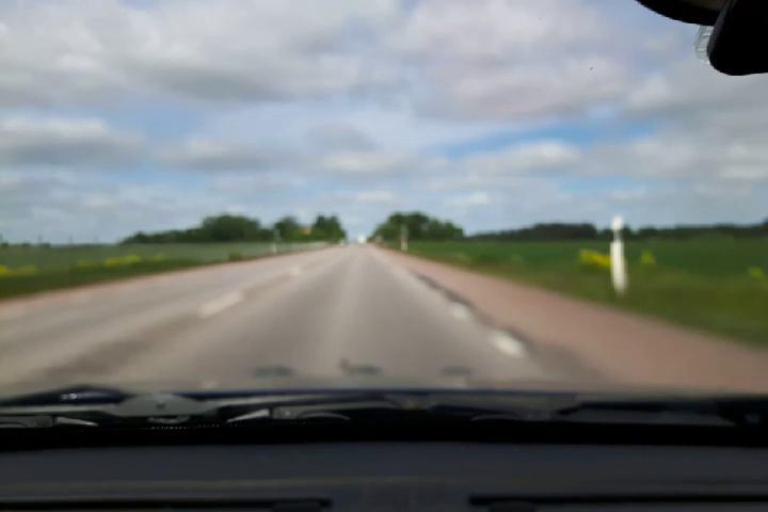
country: SE
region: Uppsala
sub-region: Uppsala Kommun
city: Gamla Uppsala
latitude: 59.9015
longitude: 17.6118
